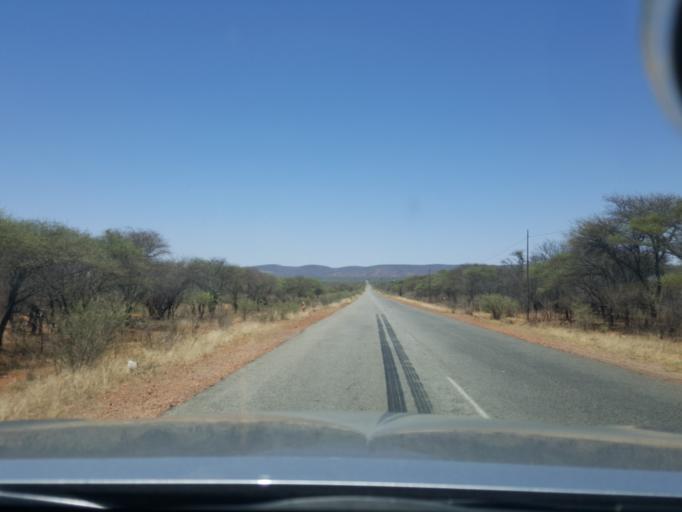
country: BW
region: South East
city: Lobatse
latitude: -25.2193
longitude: 25.9417
